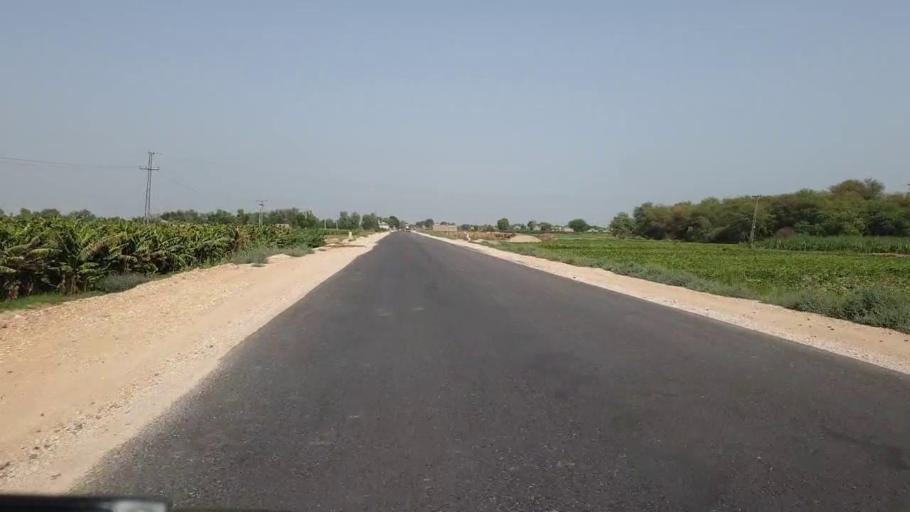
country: PK
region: Sindh
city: Sakrand
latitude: 26.2512
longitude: 68.2070
